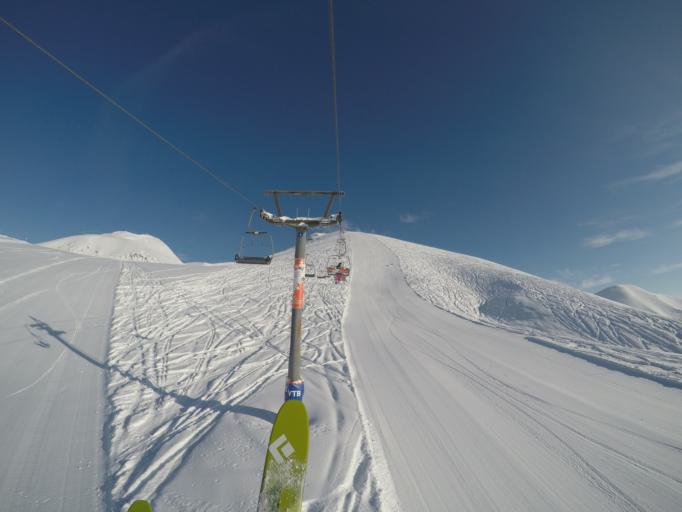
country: GE
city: Gudauri
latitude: 42.4928
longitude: 44.5033
